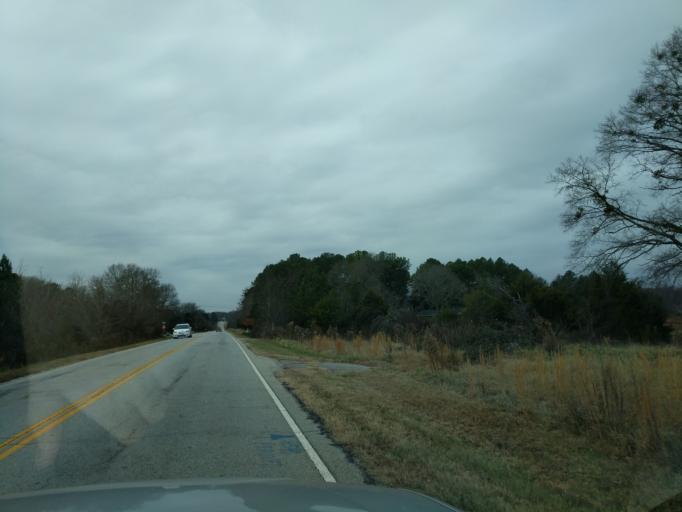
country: US
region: South Carolina
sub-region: Spartanburg County
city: Wellford
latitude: 34.8693
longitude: -82.0864
